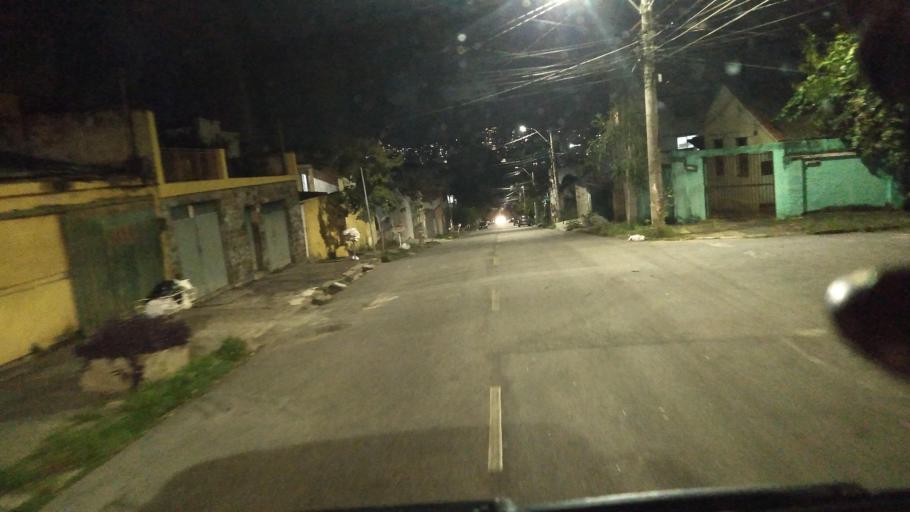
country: BR
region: Minas Gerais
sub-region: Belo Horizonte
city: Belo Horizonte
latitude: -19.9124
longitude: -43.9149
